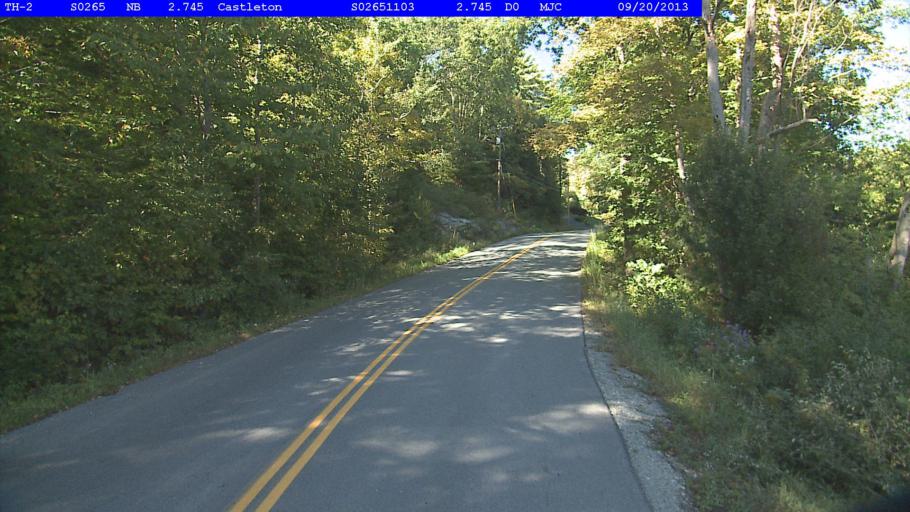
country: US
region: Vermont
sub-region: Rutland County
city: Fair Haven
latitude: 43.6405
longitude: -73.2342
